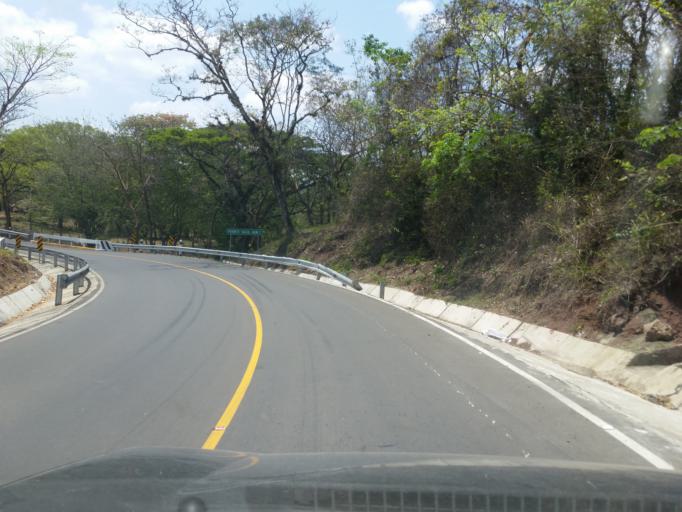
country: NI
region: Boaco
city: Boaco
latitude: 12.5416
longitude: -85.5655
